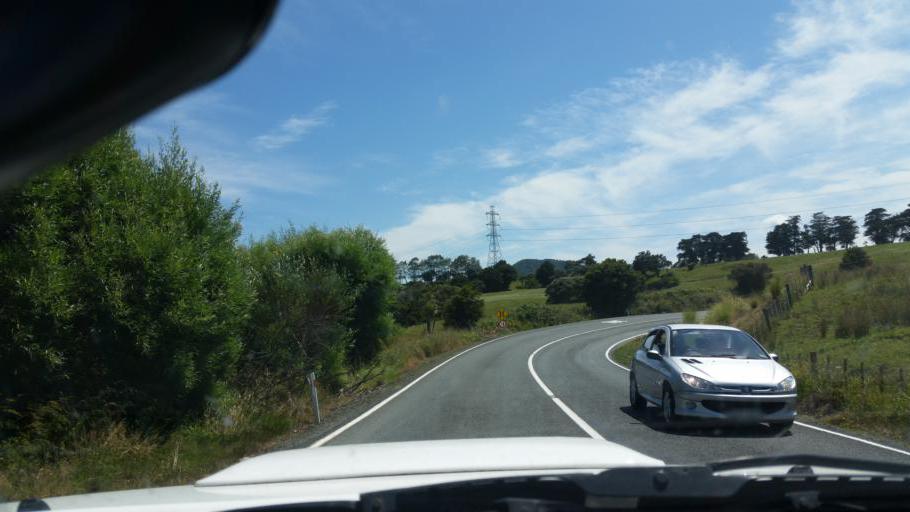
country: NZ
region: Auckland
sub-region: Auckland
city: Wellsford
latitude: -36.1657
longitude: 174.4231
